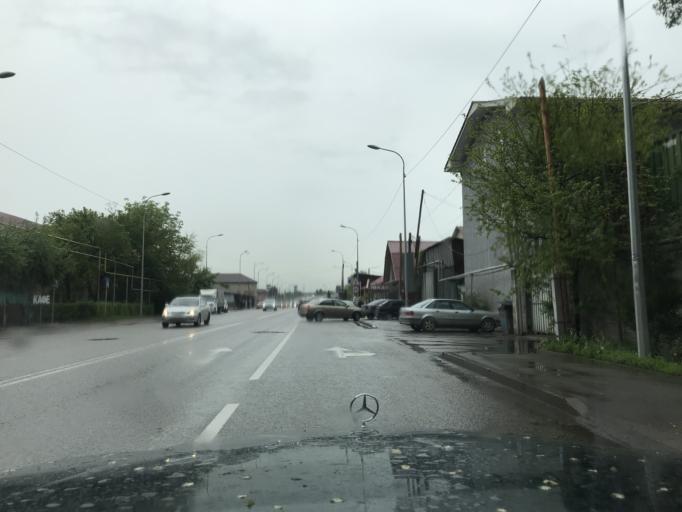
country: KZ
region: Almaty Oblysy
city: Pervomayskiy
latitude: 43.3427
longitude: 76.9669
